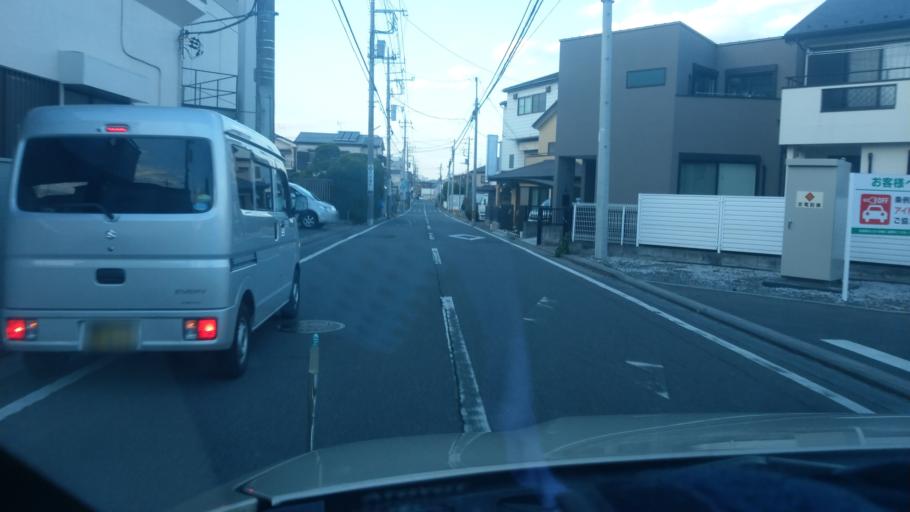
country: JP
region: Saitama
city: Yono
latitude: 35.8848
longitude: 139.6045
